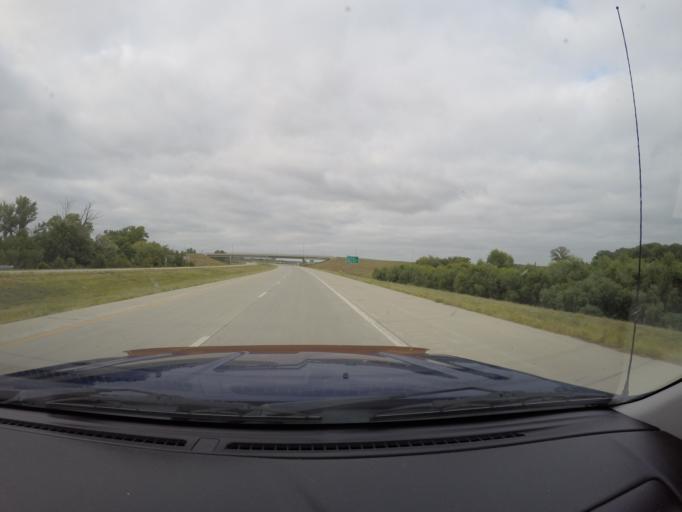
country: US
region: Kansas
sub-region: Riley County
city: Ogden
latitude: 39.1041
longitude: -96.7022
